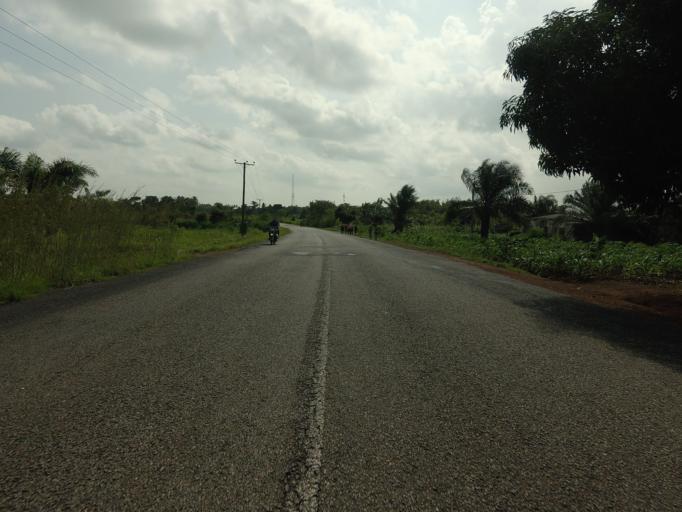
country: GH
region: Volta
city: Ho
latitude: 6.4160
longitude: 0.7535
